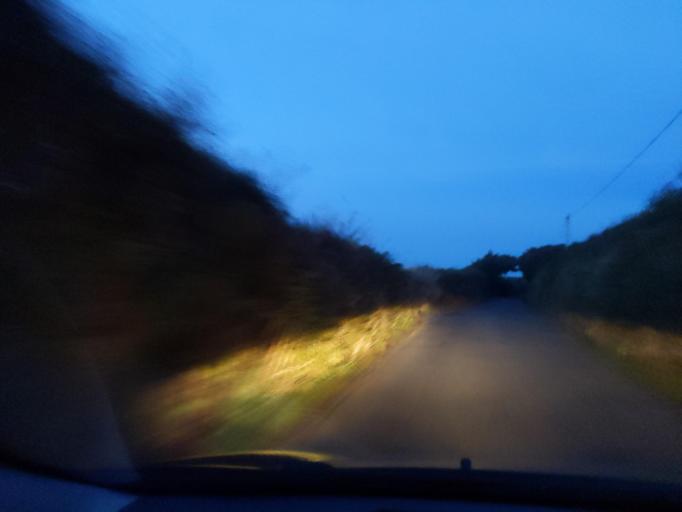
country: GB
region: England
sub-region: Cornwall
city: Camelford
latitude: 50.6988
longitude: -4.6570
